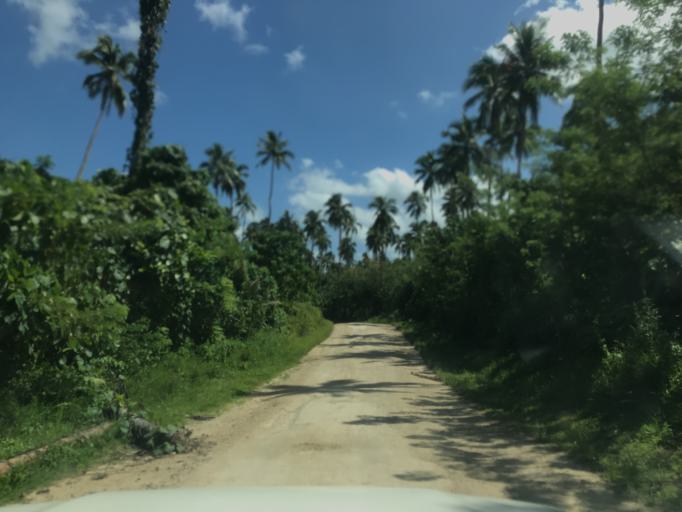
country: VU
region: Sanma
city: Luganville
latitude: -15.5784
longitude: 167.0406
